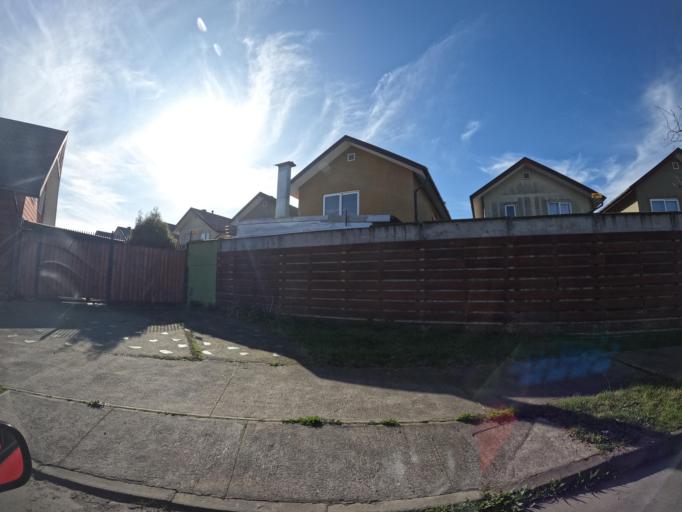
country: CL
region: Biobio
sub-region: Provincia de Concepcion
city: Concepcion
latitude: -36.7693
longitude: -73.0653
